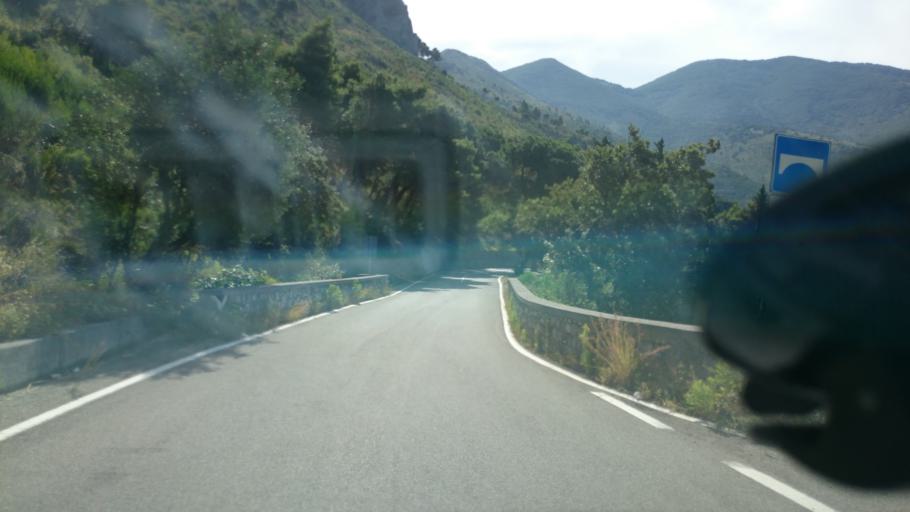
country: IT
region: Campania
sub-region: Provincia di Salerno
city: Sapri
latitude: 40.0418
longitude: 15.6674
